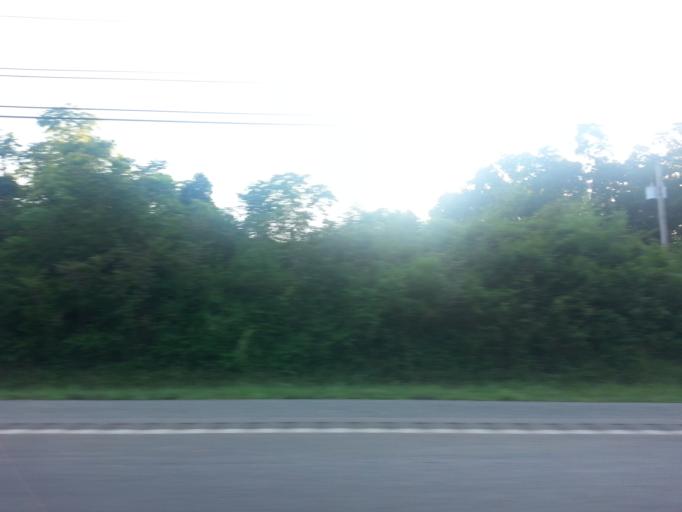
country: US
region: Tennessee
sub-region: McMinn County
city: Athens
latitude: 35.4884
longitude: -84.5996
